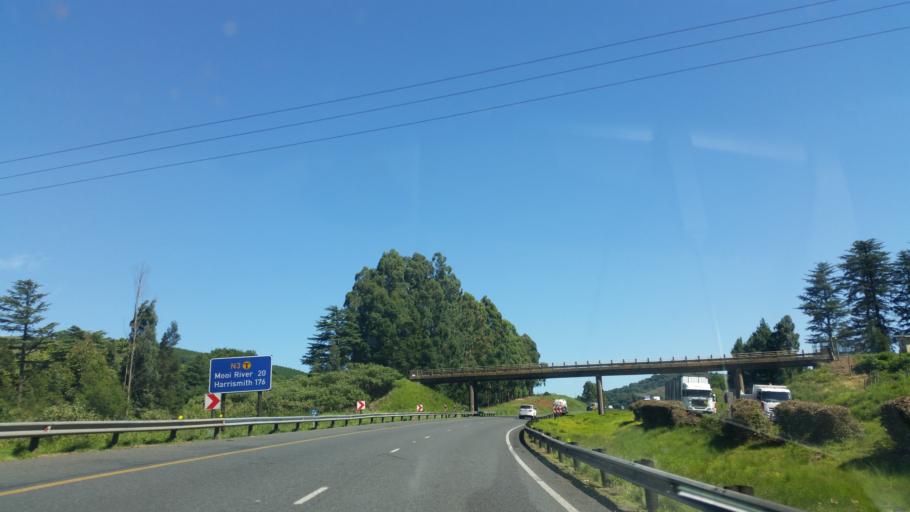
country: ZA
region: KwaZulu-Natal
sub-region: uMgungundlovu District Municipality
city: Mooirivier
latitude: -29.3547
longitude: 30.0891
